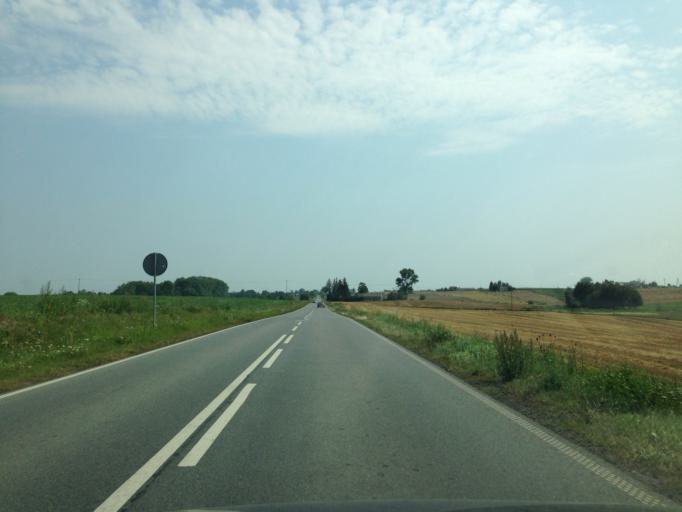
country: PL
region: Kujawsko-Pomorskie
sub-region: Powiat golubsko-dobrzynski
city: Radomin
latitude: 53.0846
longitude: 19.2166
